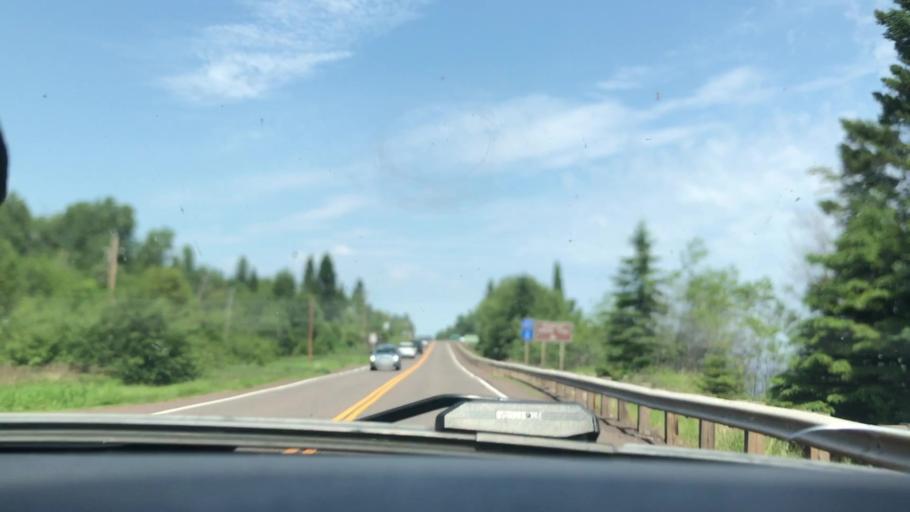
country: US
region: Minnesota
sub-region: Lake County
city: Silver Bay
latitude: 47.5748
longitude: -90.8347
